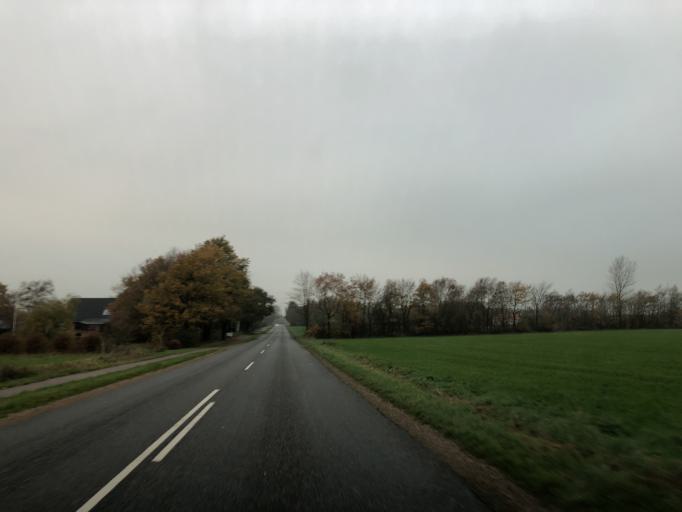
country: DK
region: Central Jutland
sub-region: Herning Kommune
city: Vildbjerg
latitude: 56.2109
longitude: 8.7535
